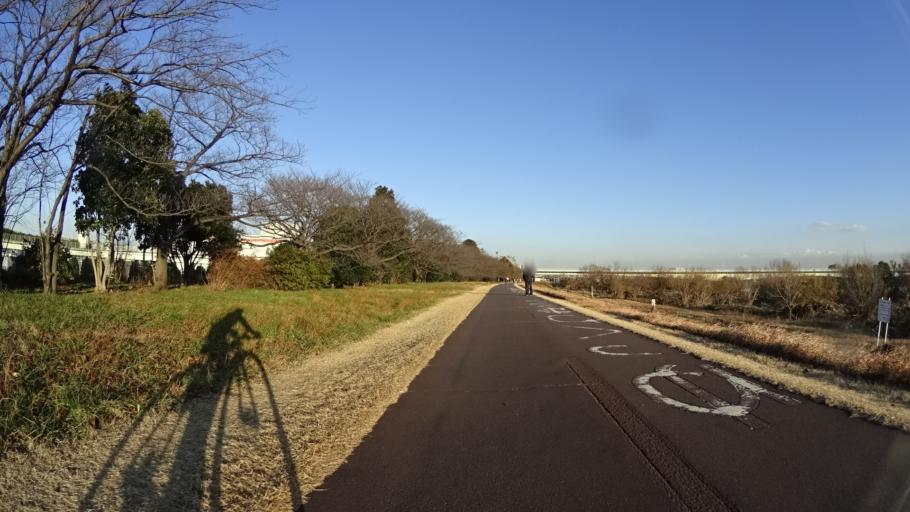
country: JP
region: Tokyo
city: Chofugaoka
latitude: 35.6537
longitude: 139.5082
